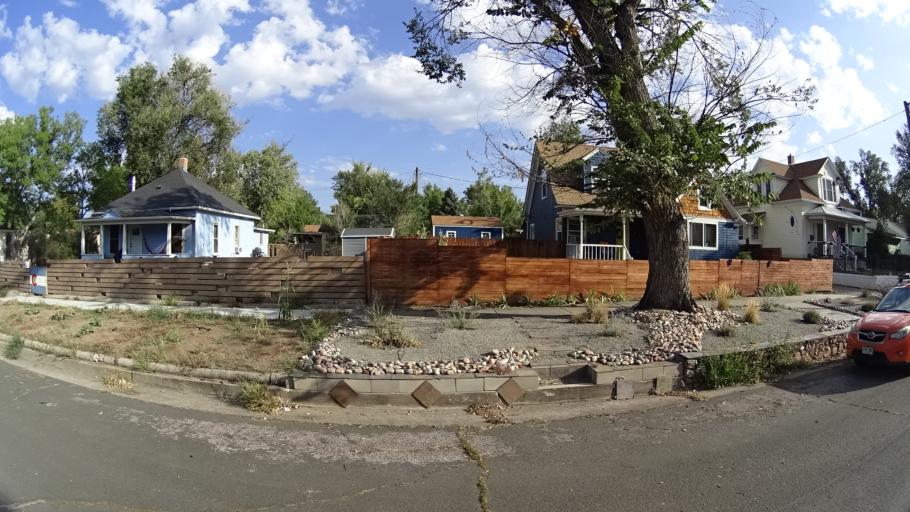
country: US
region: Colorado
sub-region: El Paso County
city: Colorado Springs
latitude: 38.8263
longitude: -104.8055
